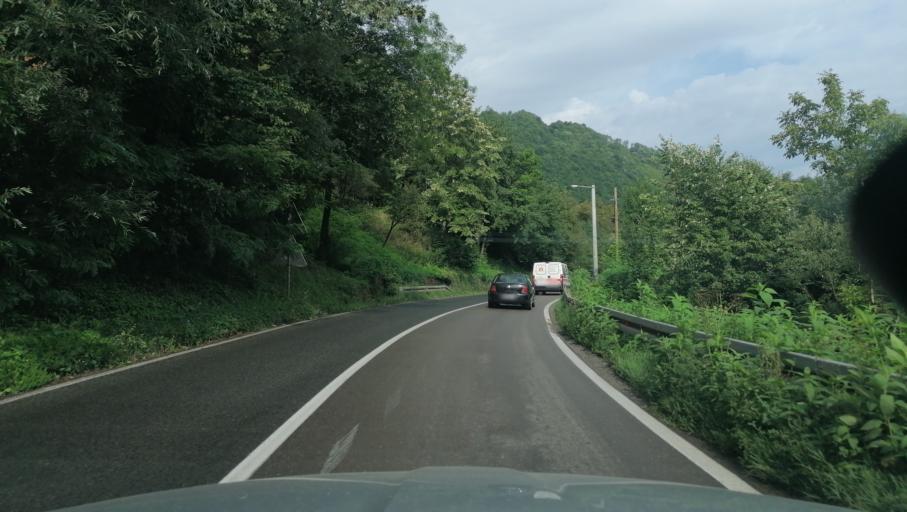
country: BA
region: Republika Srpska
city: Hiseti
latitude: 44.7188
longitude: 17.1623
